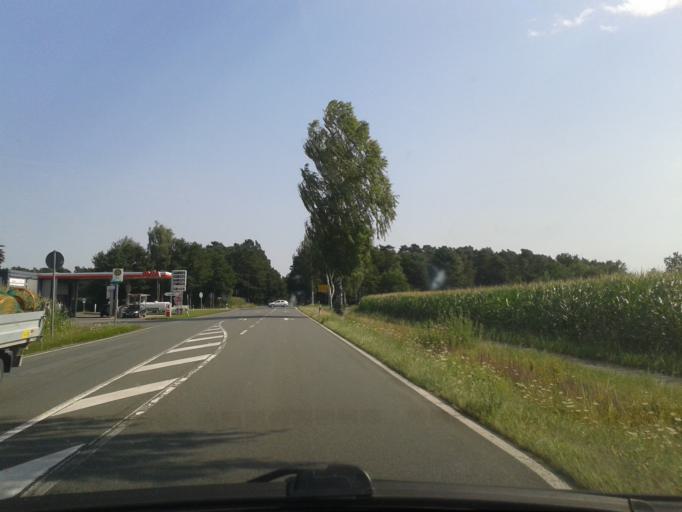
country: DE
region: North Rhine-Westphalia
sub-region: Regierungsbezirk Detmold
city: Hovelhof
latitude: 51.8417
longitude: 8.6108
